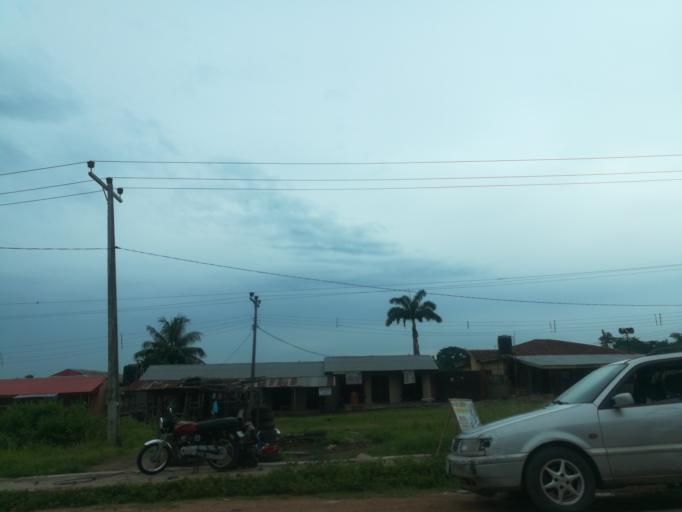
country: NG
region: Oyo
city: Egbeda
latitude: 7.3854
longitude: 4.0016
